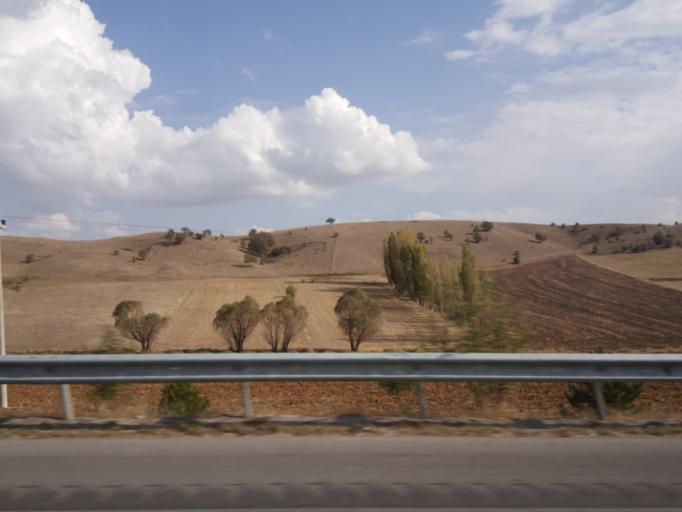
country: TR
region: Corum
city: Alaca
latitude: 40.2871
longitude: 34.6499
